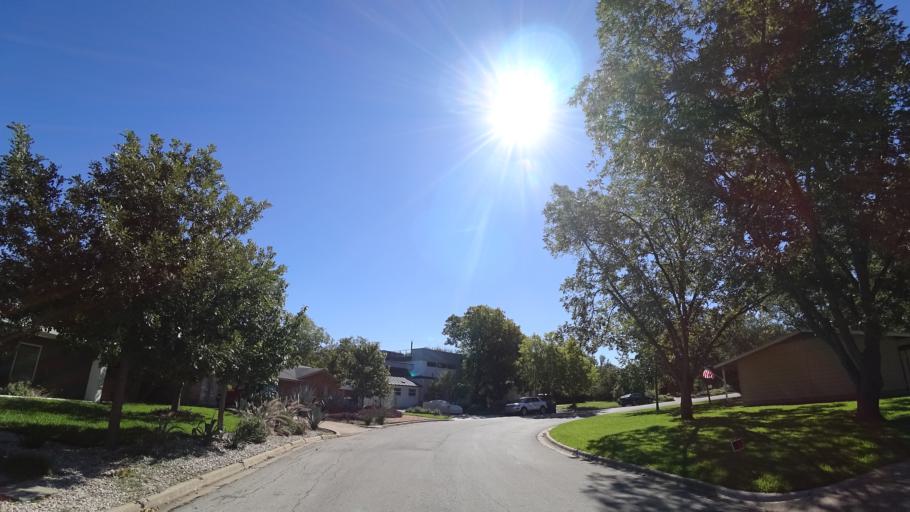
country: US
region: Texas
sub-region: Travis County
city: Austin
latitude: 30.2337
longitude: -97.7512
